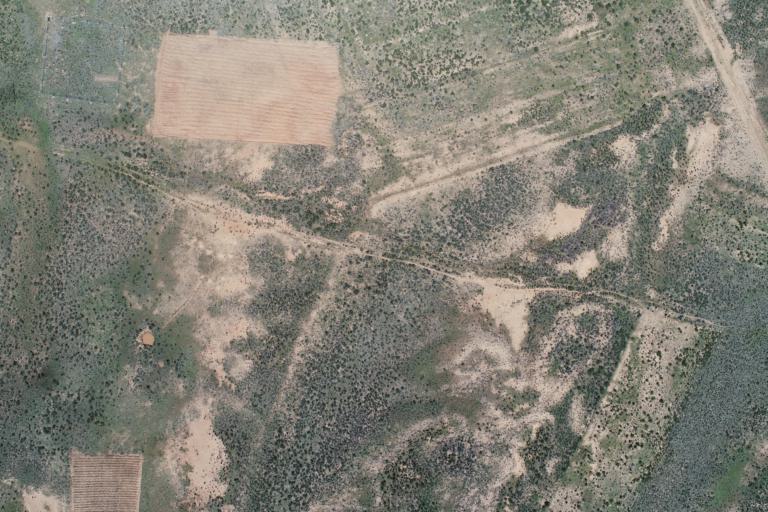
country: BO
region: La Paz
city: Curahuara de Carangas
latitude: -17.2972
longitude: -68.4959
